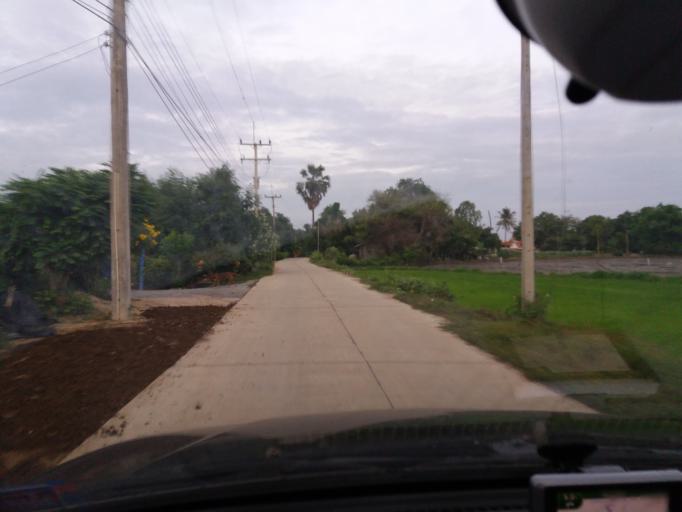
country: TH
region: Suphan Buri
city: Ban Sam Chuk
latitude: 14.7140
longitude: 100.0419
